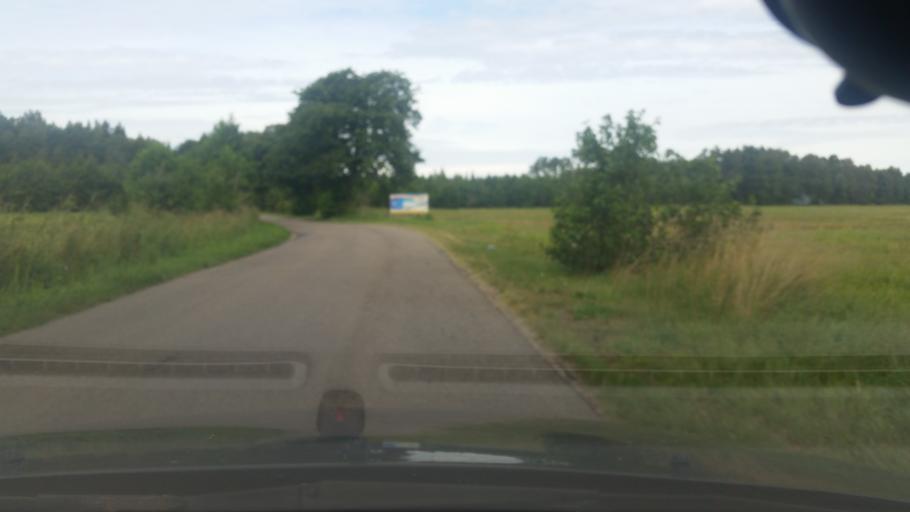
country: PL
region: Pomeranian Voivodeship
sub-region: Powiat leborski
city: Leba
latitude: 54.7369
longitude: 17.5976
